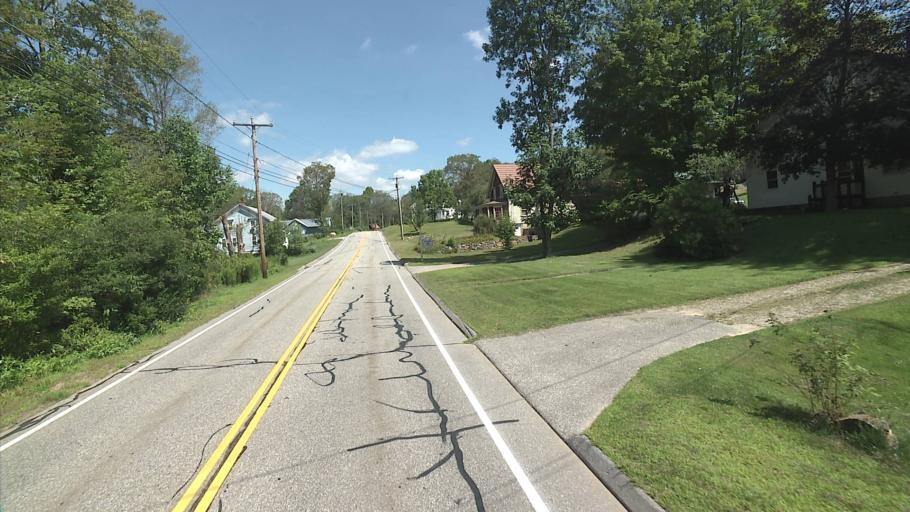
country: US
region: Connecticut
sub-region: Windham County
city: South Woodstock
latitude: 41.9048
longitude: -72.0792
